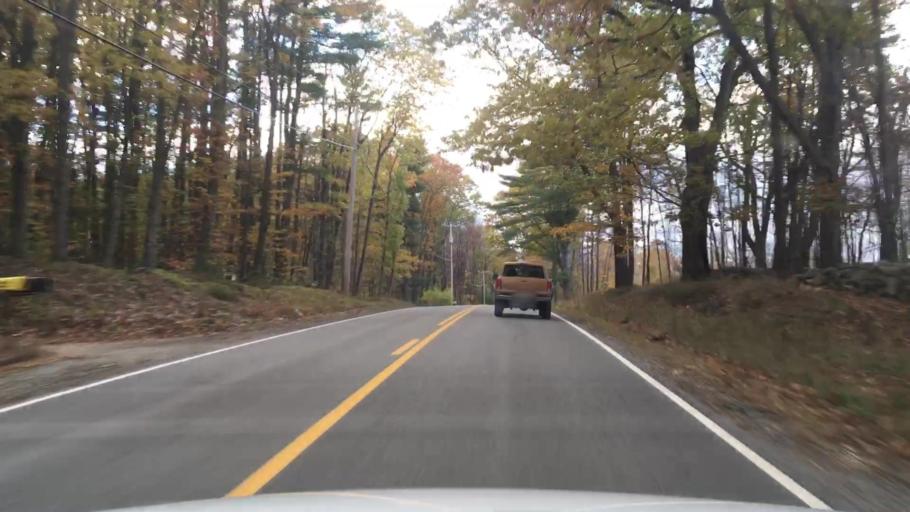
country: US
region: Maine
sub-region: Androscoggin County
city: Livermore
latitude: 44.3373
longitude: -70.2359
